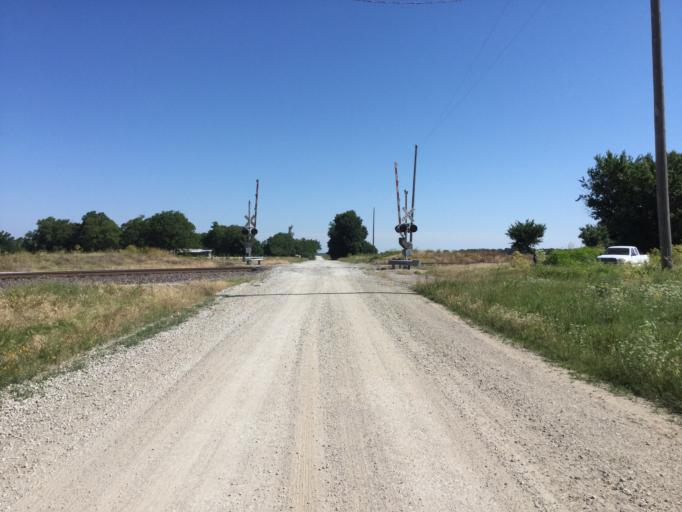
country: US
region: Kansas
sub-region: Montgomery County
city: Independence
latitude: 37.1777
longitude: -95.7469
